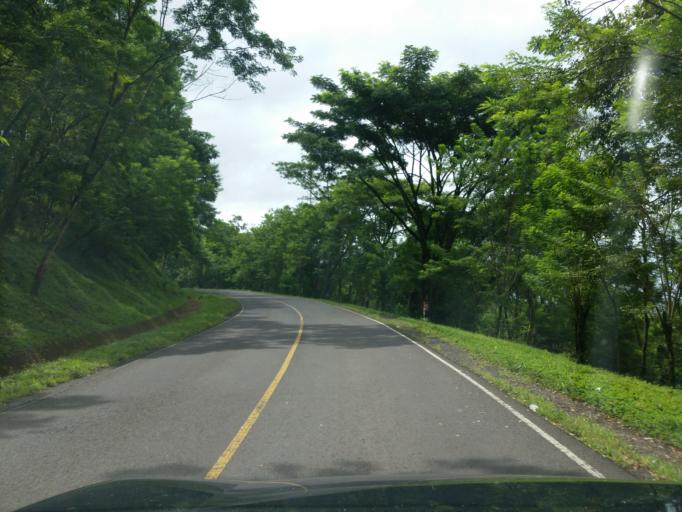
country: NI
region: Matagalpa
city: San Ramon
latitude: 13.0943
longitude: -85.7446
